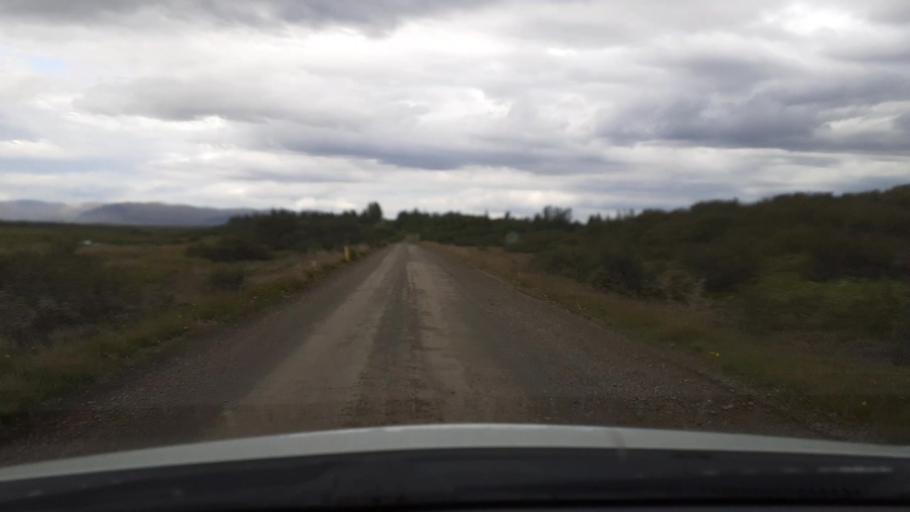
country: IS
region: West
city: Borgarnes
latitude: 64.6121
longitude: -21.9523
